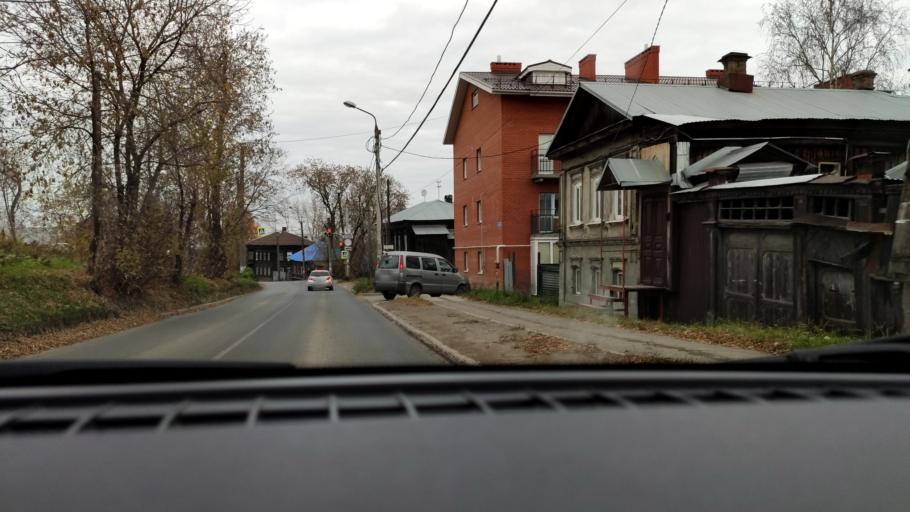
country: RU
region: Perm
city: Perm
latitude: 58.0333
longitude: 56.3129
